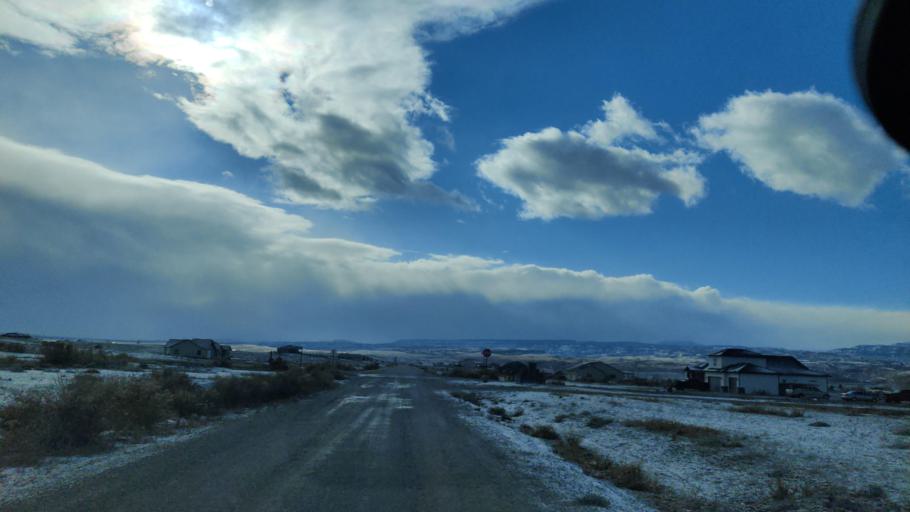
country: US
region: Colorado
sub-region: Mesa County
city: Clifton
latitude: 39.0022
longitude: -108.4249
